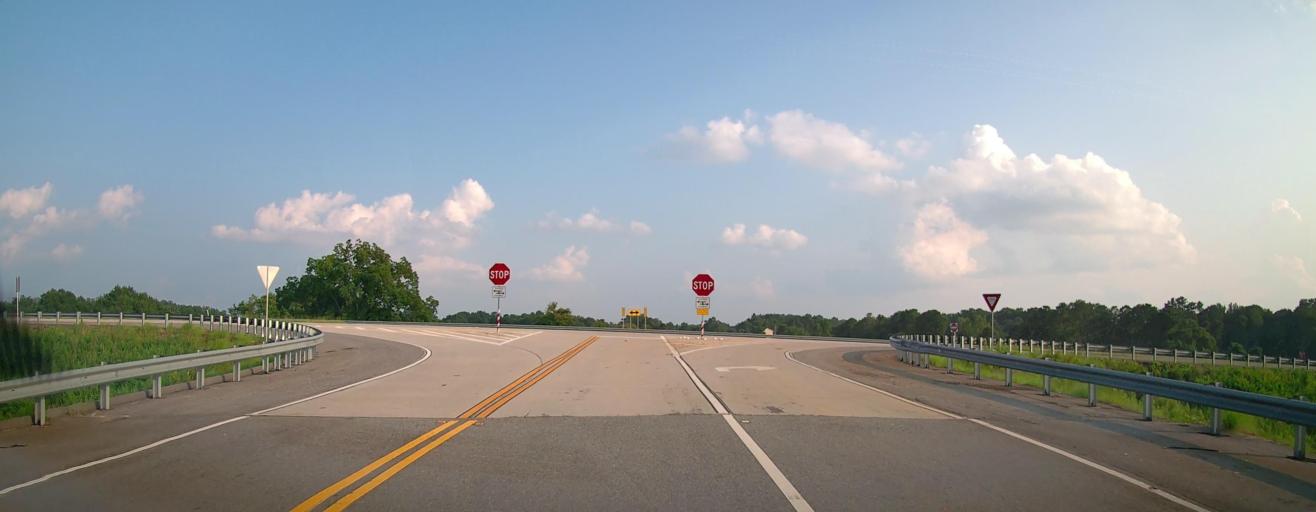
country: US
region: Georgia
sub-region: Jones County
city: Gray
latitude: 33.0292
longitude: -83.5401
